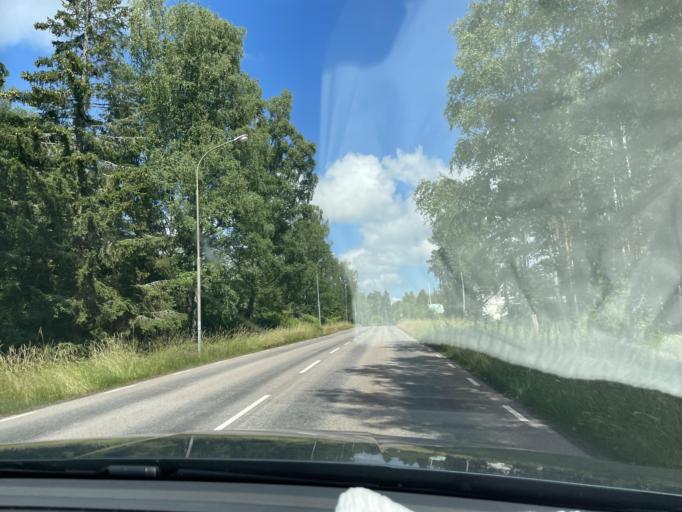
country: SE
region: Kronoberg
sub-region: Vaxjo Kommun
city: Vaexjoe
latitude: 56.8570
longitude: 14.8441
